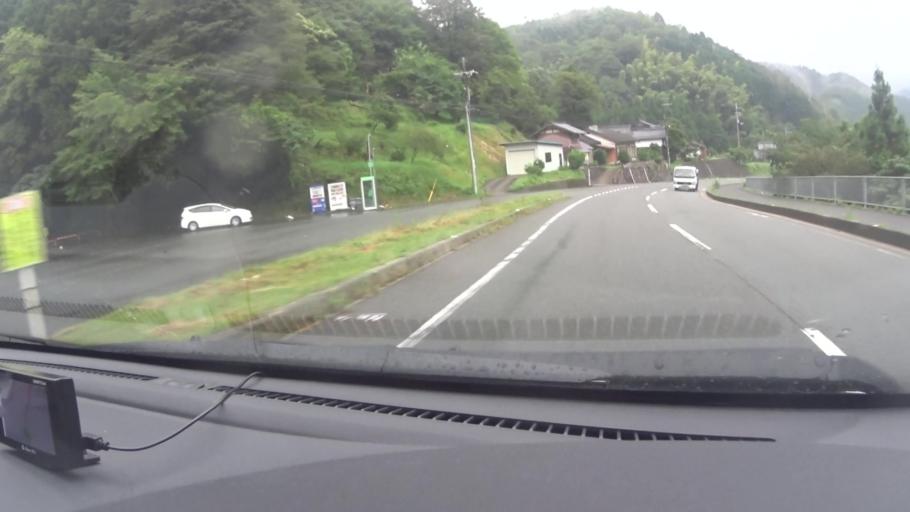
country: JP
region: Kyoto
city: Ayabe
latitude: 35.2594
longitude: 135.2754
